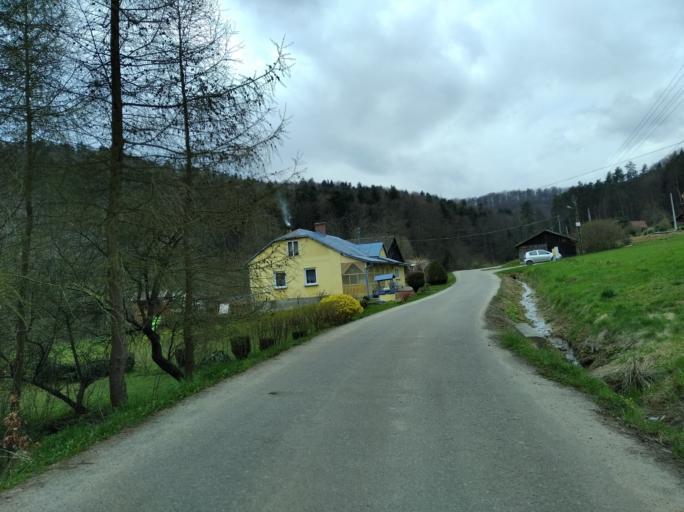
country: PL
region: Subcarpathian Voivodeship
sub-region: Powiat strzyzowski
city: Wysoka Strzyzowska
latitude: 49.8297
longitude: 21.7045
